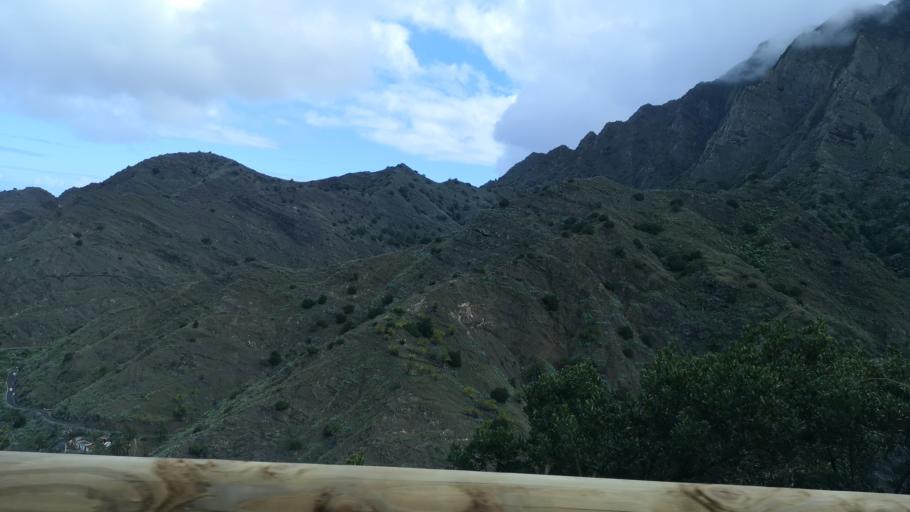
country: ES
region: Canary Islands
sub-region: Provincia de Santa Cruz de Tenerife
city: Hermigua
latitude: 28.1428
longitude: -17.1980
